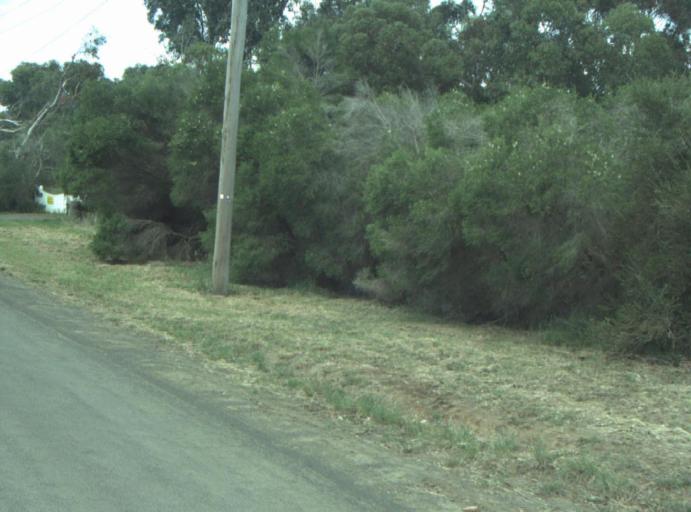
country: AU
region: Victoria
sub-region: Greater Geelong
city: Clifton Springs
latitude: -38.1960
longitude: 144.5663
